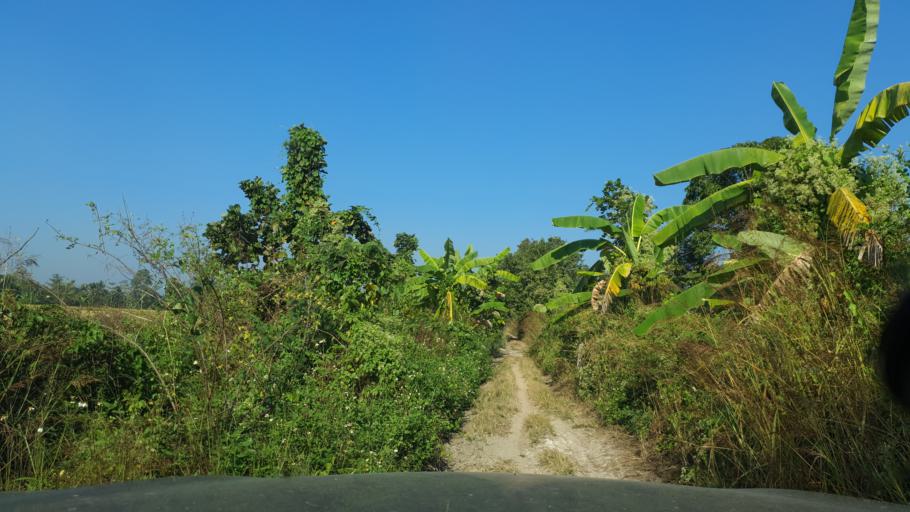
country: TH
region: Chiang Mai
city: Saraphi
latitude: 18.7111
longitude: 99.0792
